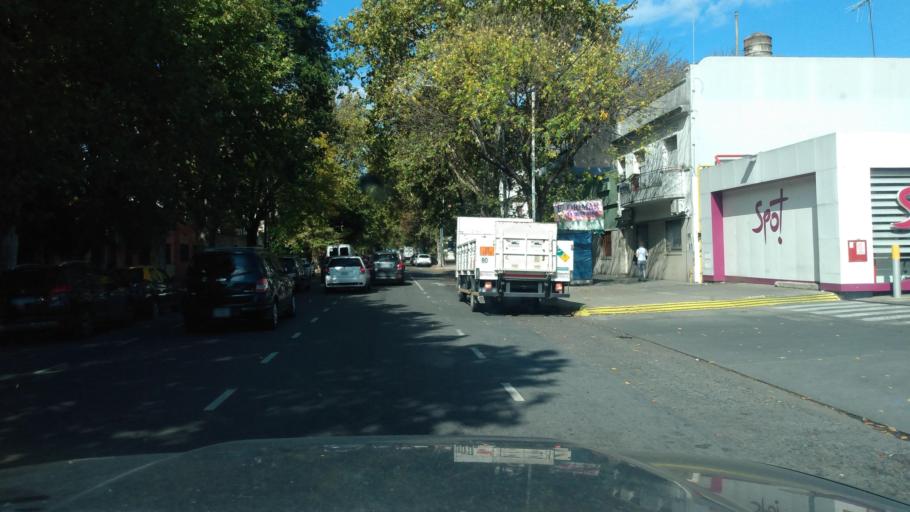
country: AR
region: Buenos Aires
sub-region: Partido de General San Martin
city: General San Martin
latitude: -34.5638
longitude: -58.4964
